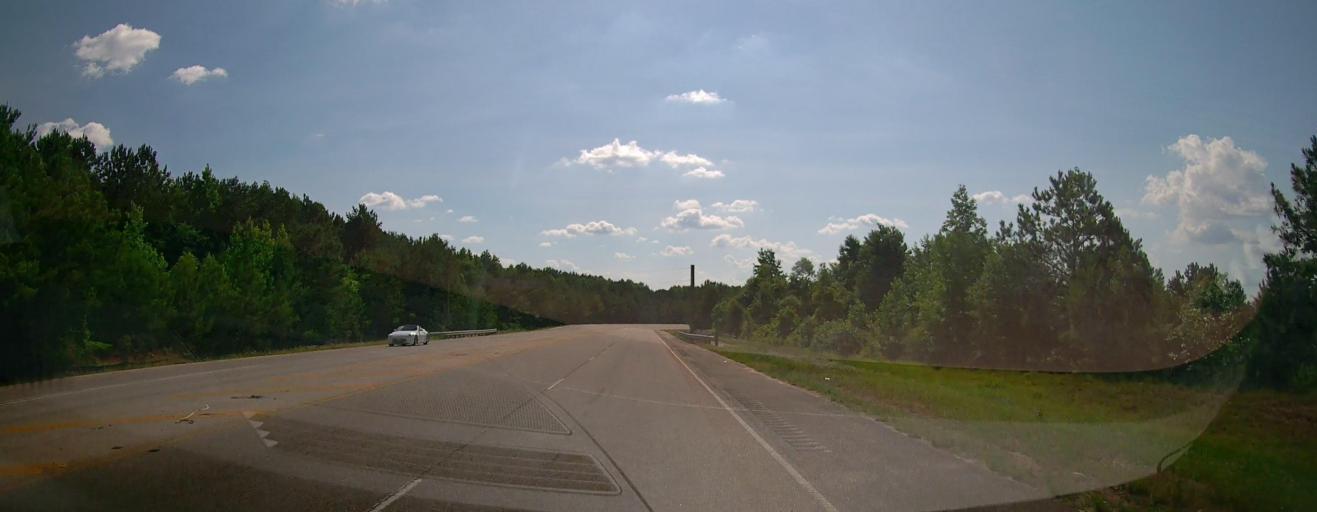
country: US
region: Georgia
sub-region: Henry County
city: Hampton
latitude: 33.3699
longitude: -84.2996
